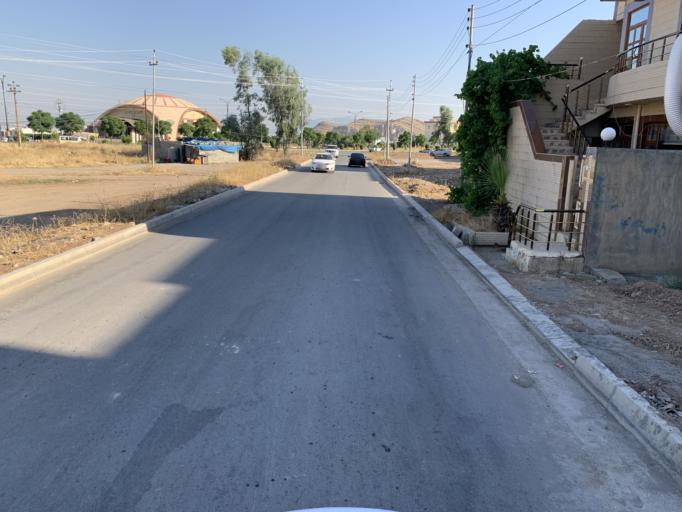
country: IQ
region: As Sulaymaniyah
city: Raniye
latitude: 36.2388
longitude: 44.8715
